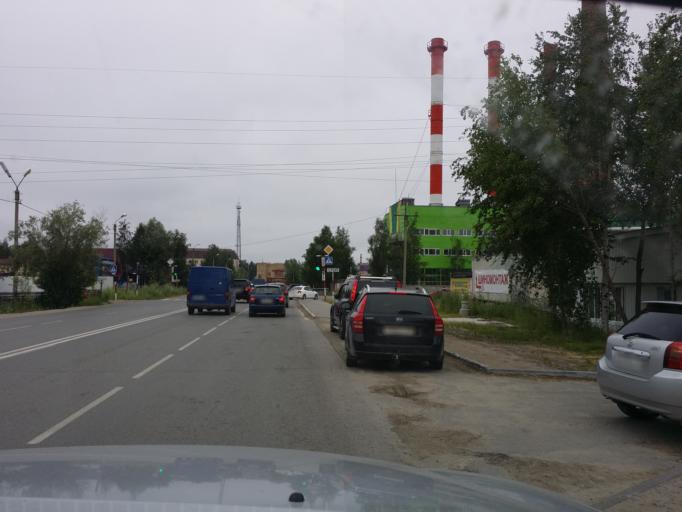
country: RU
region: Khanty-Mansiyskiy Avtonomnyy Okrug
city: Nizhnevartovsk
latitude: 60.9342
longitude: 76.5490
